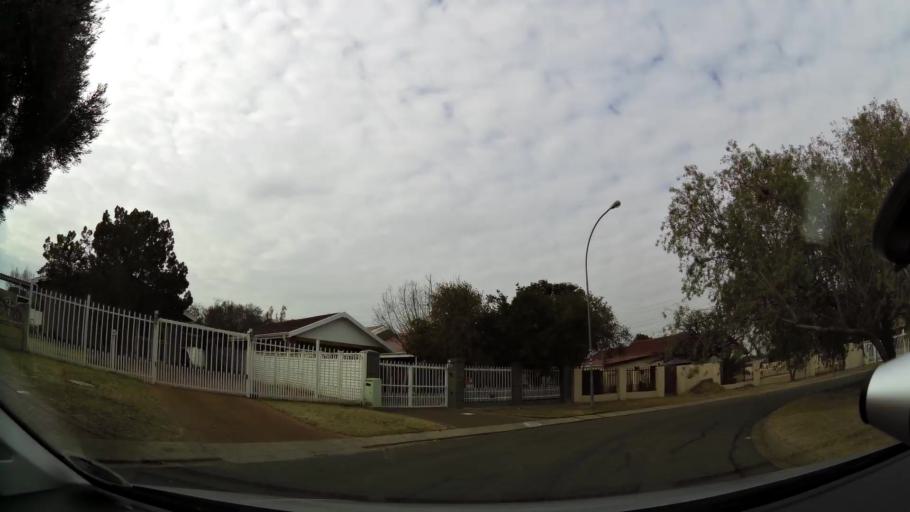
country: ZA
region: Orange Free State
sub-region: Mangaung Metropolitan Municipality
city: Bloemfontein
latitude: -29.1322
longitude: 26.1670
